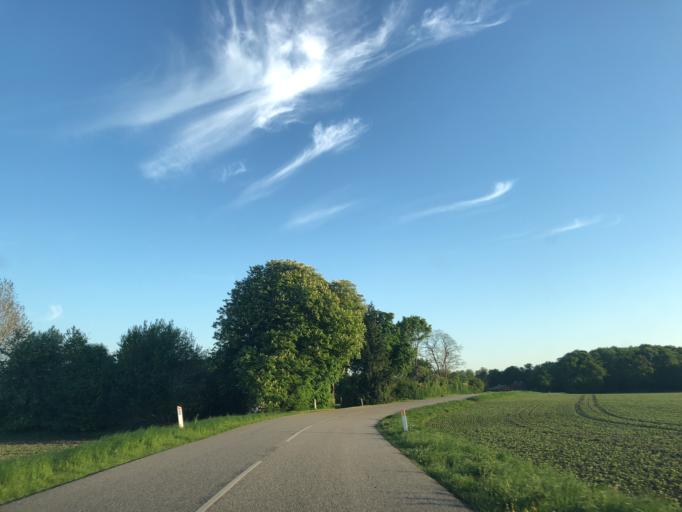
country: DK
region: Zealand
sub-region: Koge Kommune
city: Borup
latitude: 55.4393
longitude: 11.9466
